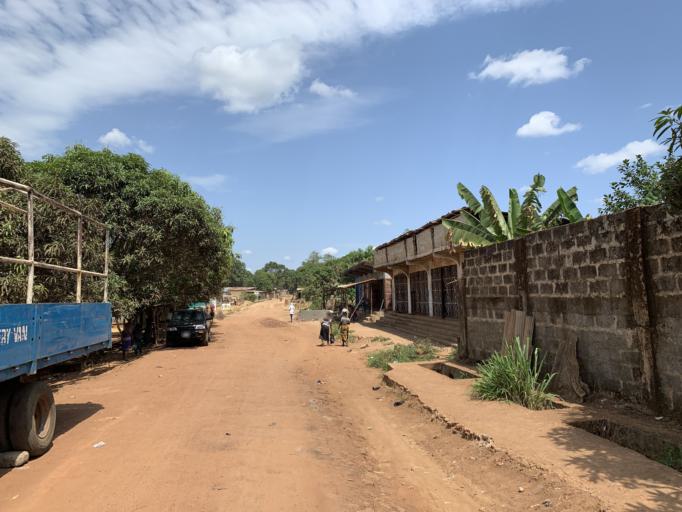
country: SL
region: Western Area
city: Waterloo
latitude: 8.3334
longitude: -13.0421
